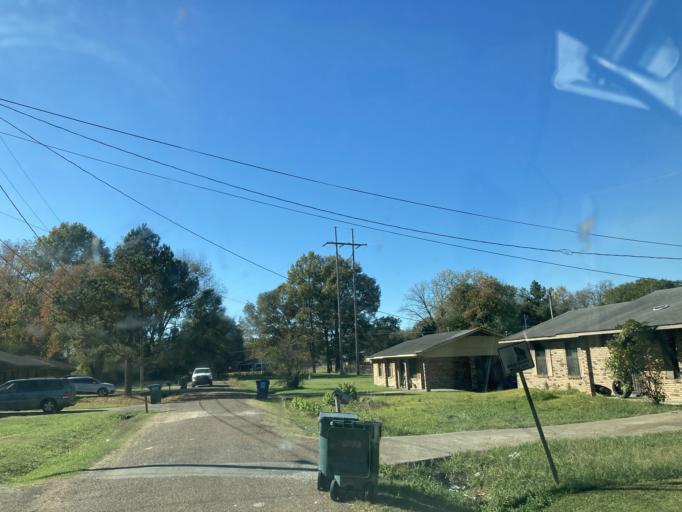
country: US
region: Mississippi
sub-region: Yazoo County
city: Yazoo City
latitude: 32.8425
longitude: -90.4233
